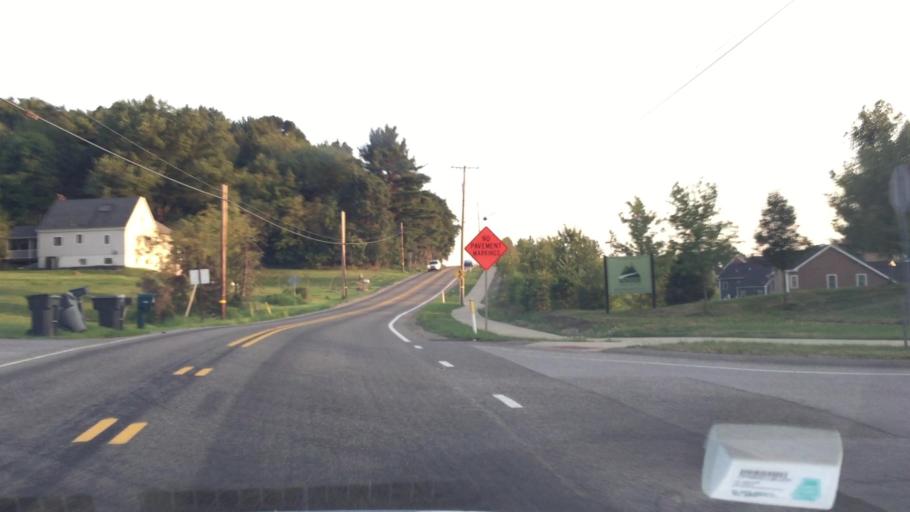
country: US
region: Pennsylvania
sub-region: Butler County
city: Fox Run
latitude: 40.7182
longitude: -80.0766
